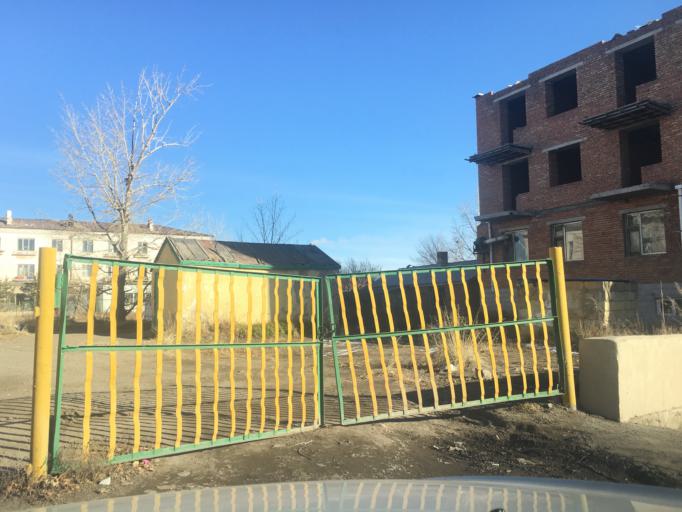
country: MN
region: Ulaanbaatar
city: Ulaanbaatar
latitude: 47.9074
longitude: 106.7947
